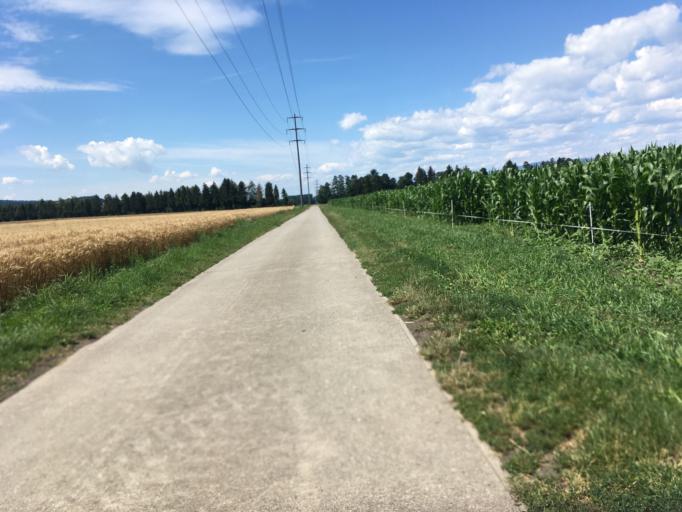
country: CH
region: Fribourg
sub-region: See District
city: Bas-Vully
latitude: 46.9661
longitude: 7.0556
